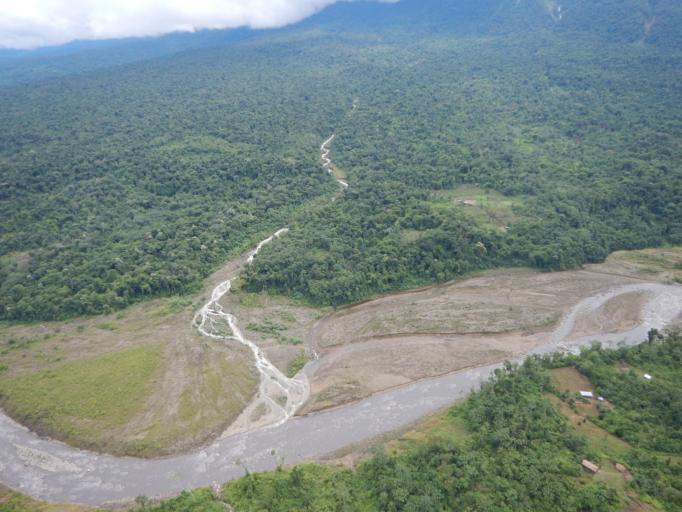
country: BO
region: Cochabamba
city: Totora
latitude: -17.3797
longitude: -65.1203
